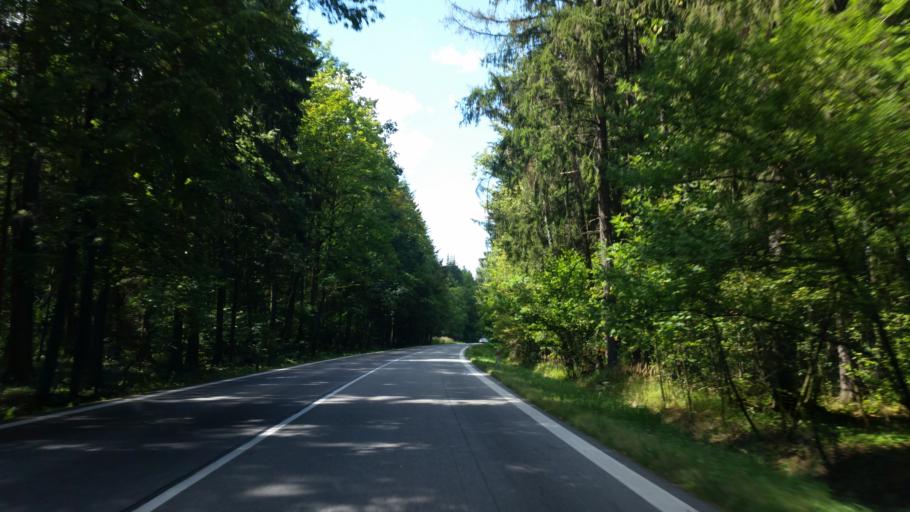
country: CZ
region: Vysocina
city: Cernovice
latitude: 49.4214
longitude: 14.9682
